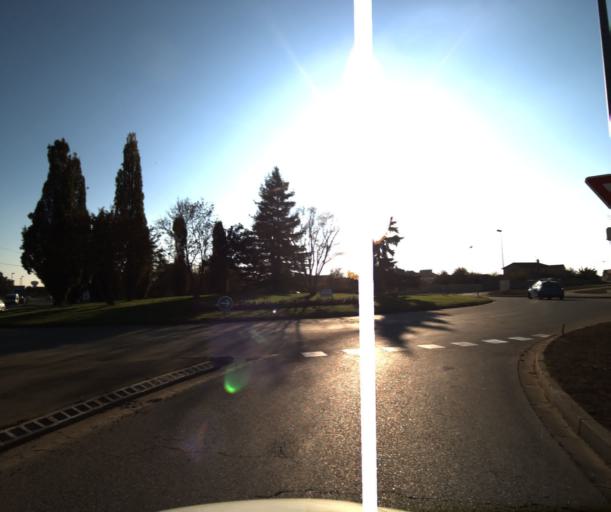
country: FR
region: Midi-Pyrenees
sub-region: Departement de la Haute-Garonne
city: Colomiers
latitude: 43.6249
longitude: 1.3327
